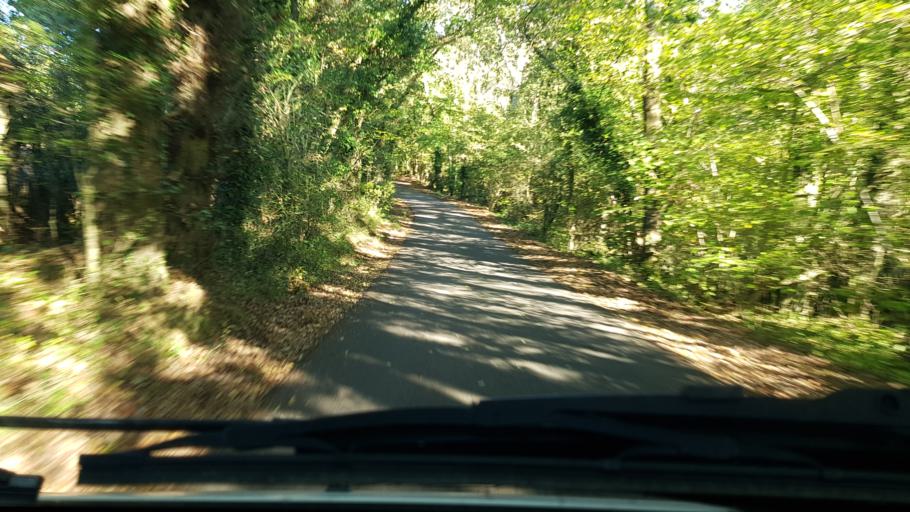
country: GB
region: England
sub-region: Surrey
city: Ockley
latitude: 51.1296
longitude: -0.3499
